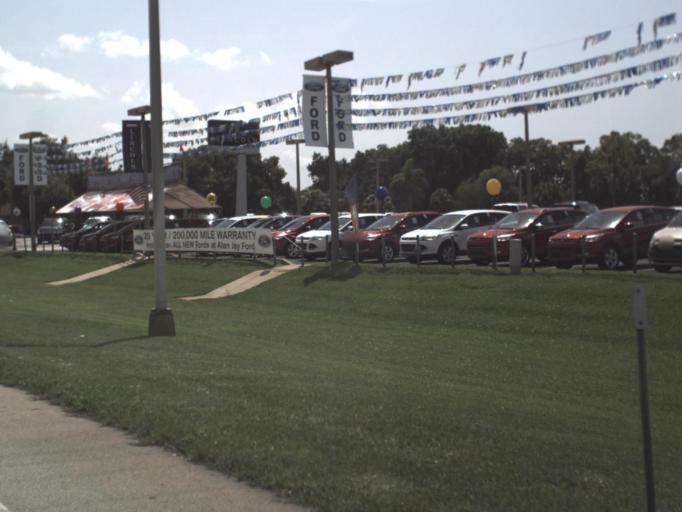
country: US
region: Florida
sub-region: Highlands County
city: Sebring
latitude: 27.4696
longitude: -81.4406
